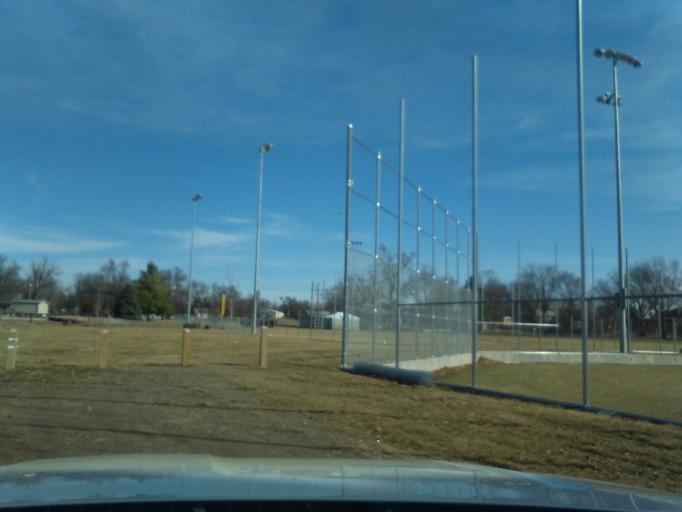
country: US
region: Nebraska
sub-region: Saline County
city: Friend
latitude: 40.7766
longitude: -97.2768
